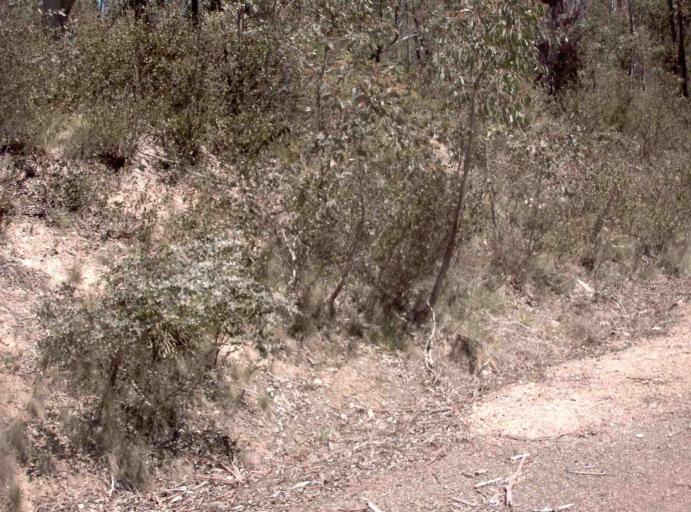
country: AU
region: New South Wales
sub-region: Snowy River
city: Jindabyne
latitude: -37.1142
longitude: 148.2421
